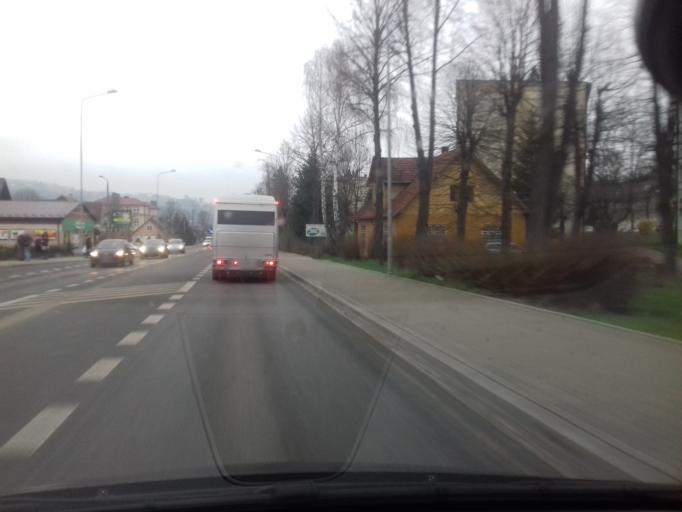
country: PL
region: Lesser Poland Voivodeship
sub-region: Powiat limanowski
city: Limanowa
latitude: 49.7189
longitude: 20.4104
